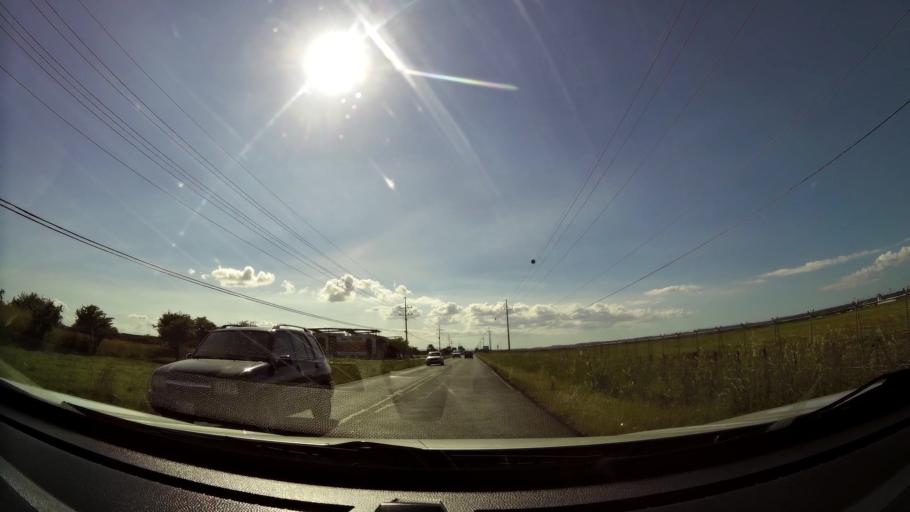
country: CR
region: Guanacaste
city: Liberia
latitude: 10.5948
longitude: -85.5324
